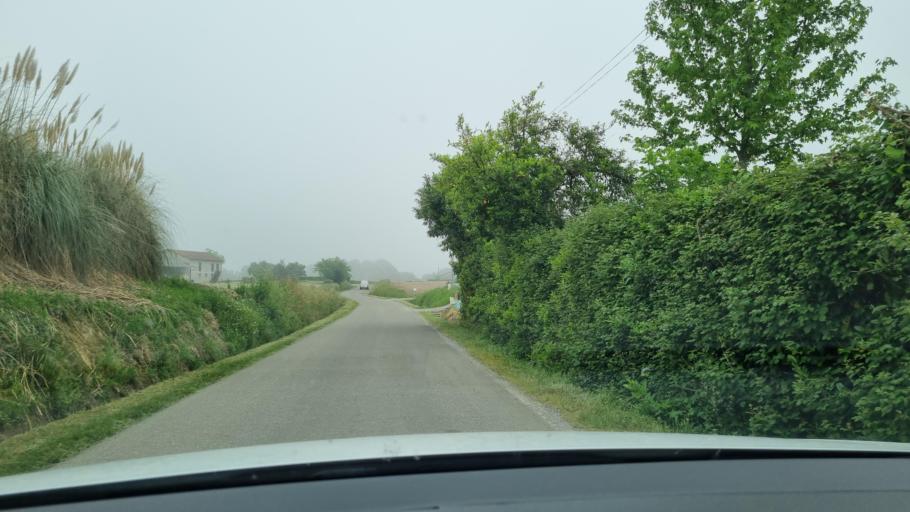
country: FR
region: Aquitaine
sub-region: Departement des Landes
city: Hagetmau
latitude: 43.6467
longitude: -0.6085
